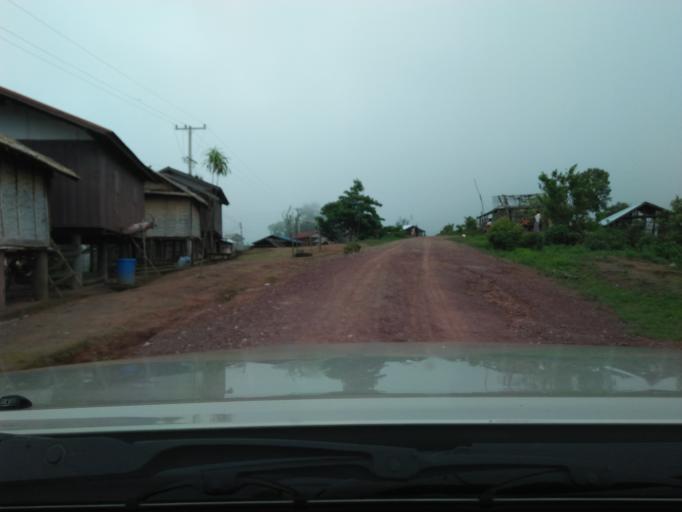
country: TH
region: Nan
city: Bo Kluea
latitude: 19.3847
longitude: 101.2392
